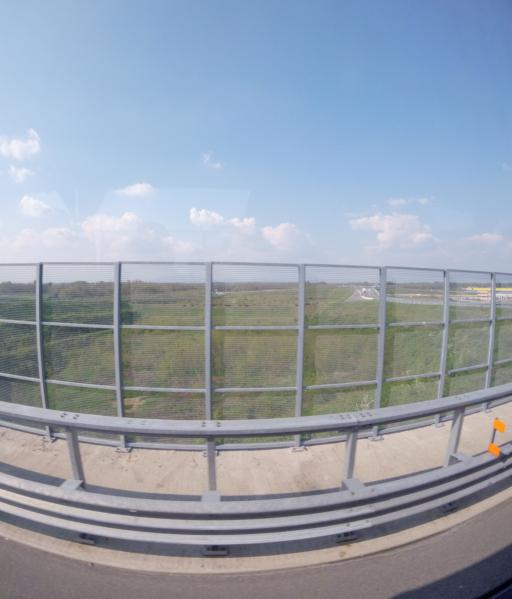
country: IT
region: Lombardy
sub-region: Provincia di Varese
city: Cassano Magnago
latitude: 45.6433
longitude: 8.8381
